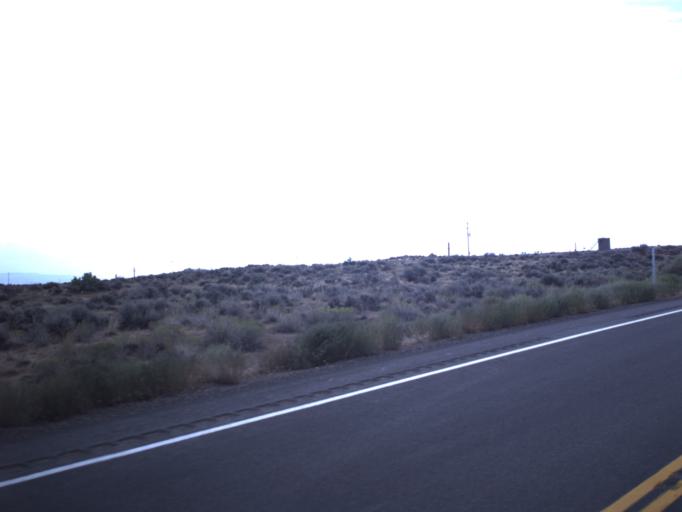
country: US
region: Utah
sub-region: Uintah County
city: Naples
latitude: 40.2075
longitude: -109.3615
